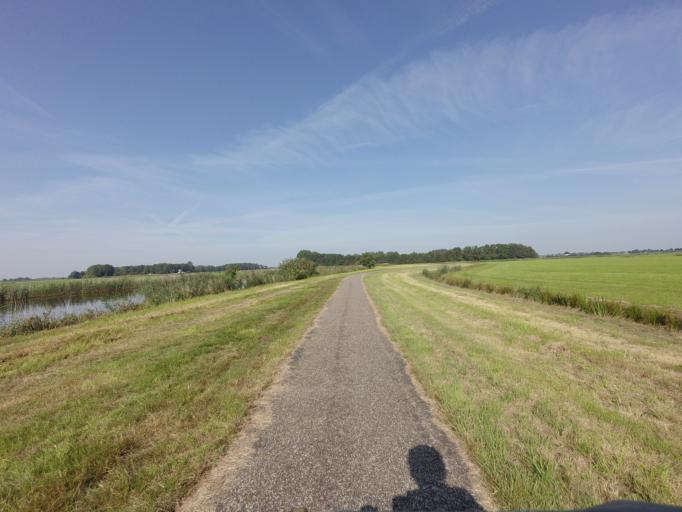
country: NL
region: Overijssel
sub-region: Gemeente Steenwijkerland
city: Oldemarkt
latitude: 52.8367
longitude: 5.9487
